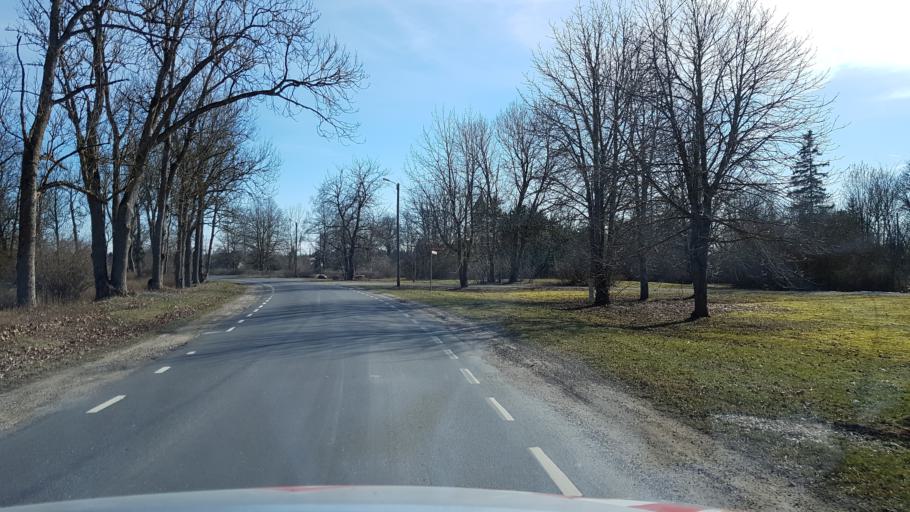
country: EE
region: Harju
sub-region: Nissi vald
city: Riisipere
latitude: 59.1038
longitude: 24.3104
